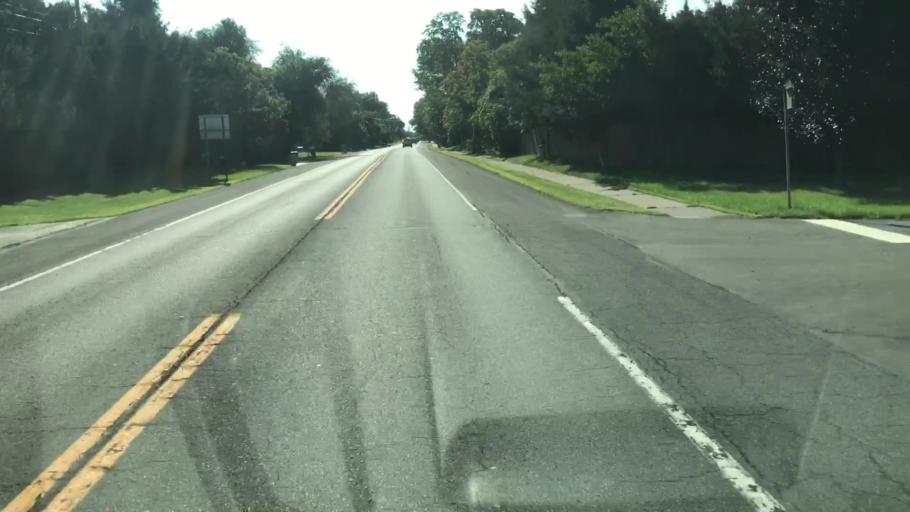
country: US
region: New York
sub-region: Onondaga County
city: Fayetteville
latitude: 43.0109
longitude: -75.9969
